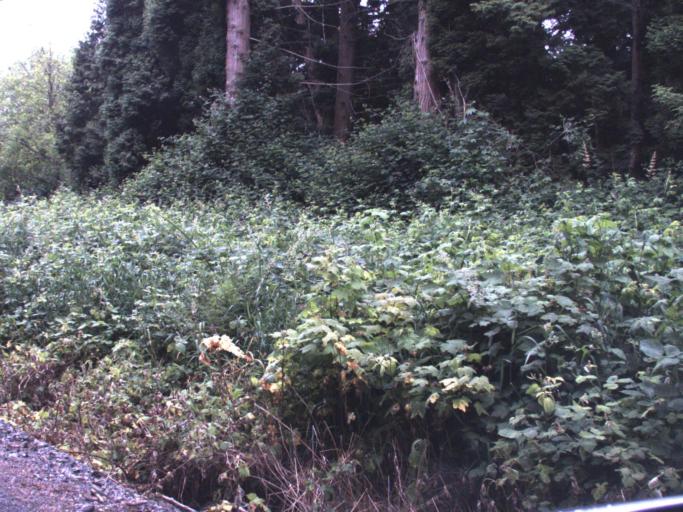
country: US
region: Washington
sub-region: Whatcom County
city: Birch Bay
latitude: 48.9025
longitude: -122.7266
